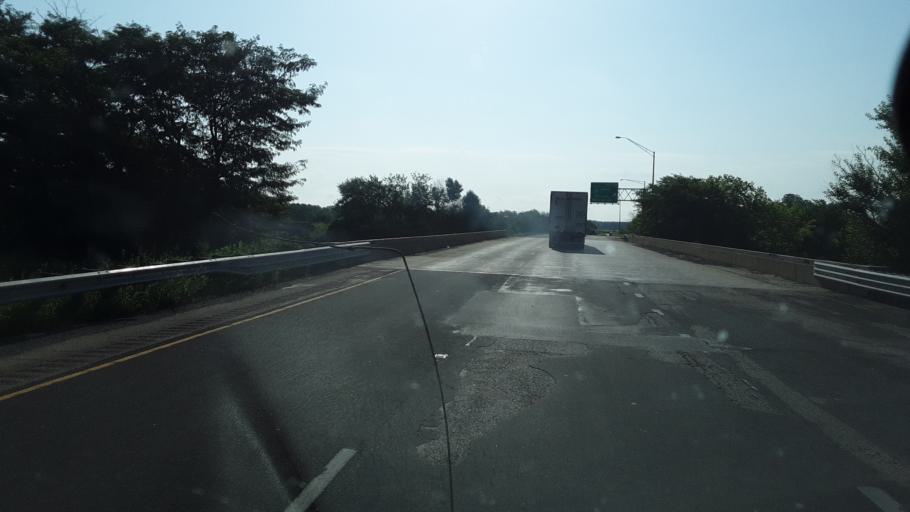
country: US
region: Illinois
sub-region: Madison County
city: Troy
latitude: 38.7521
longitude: -89.9082
